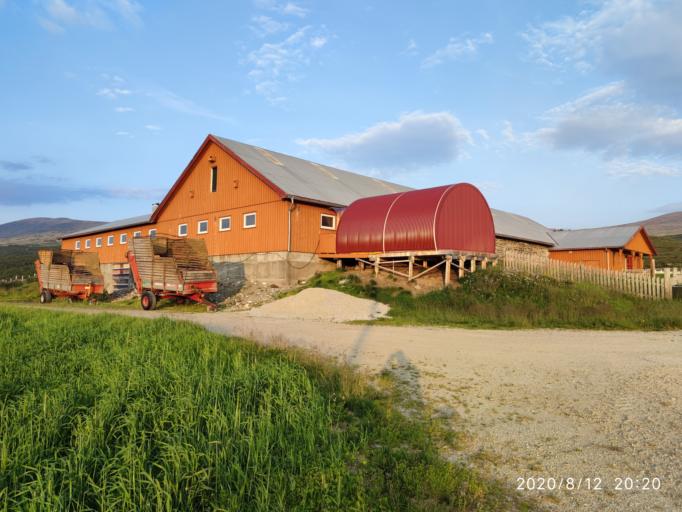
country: NO
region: Oppland
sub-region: Dovre
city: Dovre
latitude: 62.1147
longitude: 9.2858
